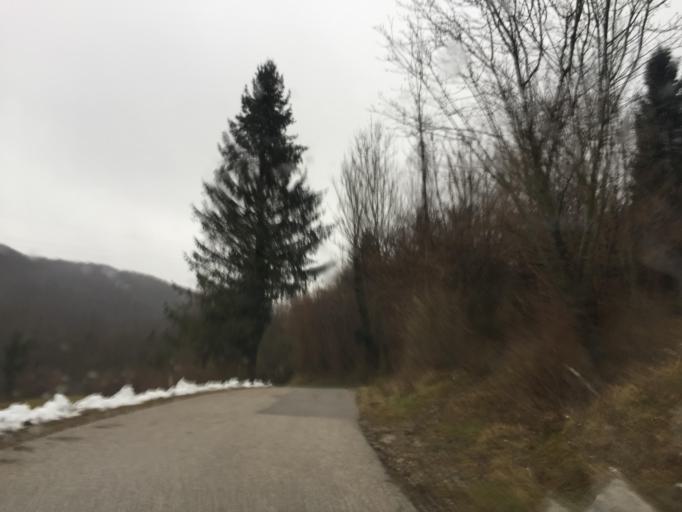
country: SI
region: Kanal
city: Kanal
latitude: 46.0733
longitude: 13.6651
